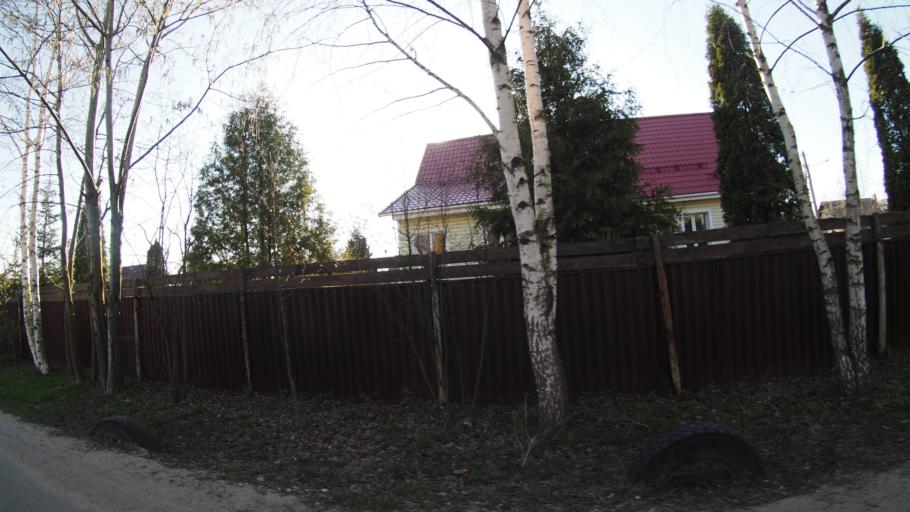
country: RU
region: Moskovskaya
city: Malyshevo
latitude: 55.5029
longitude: 38.3399
